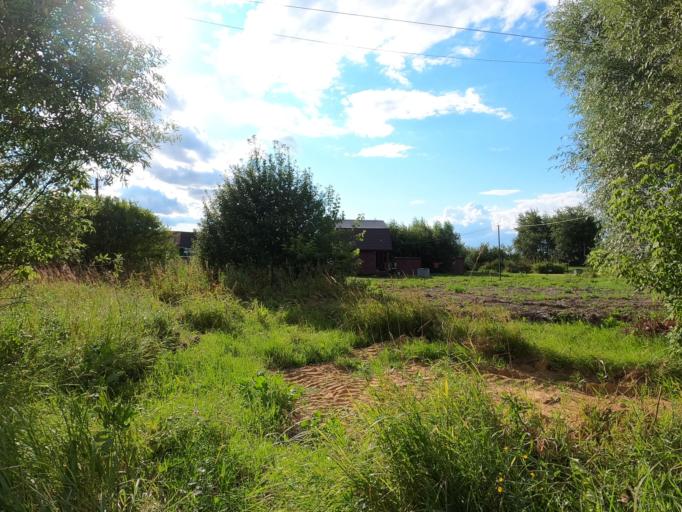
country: RU
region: Moskovskaya
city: Konobeyevo
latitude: 55.4093
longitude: 38.7179
